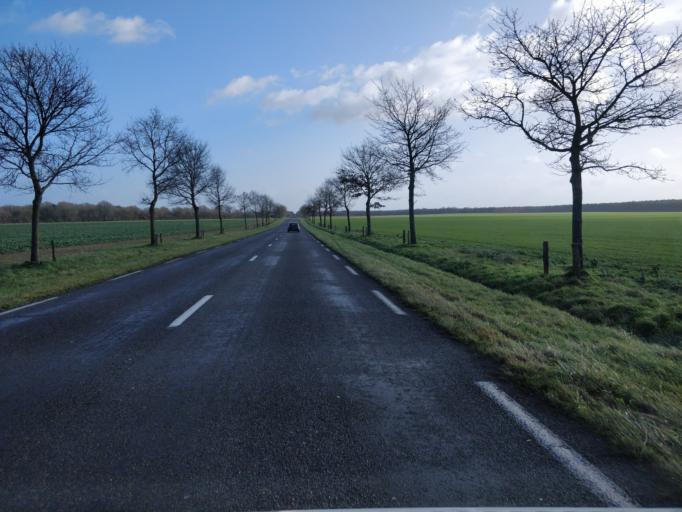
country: FR
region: Ile-de-France
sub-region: Departement de Seine-et-Marne
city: Bagneaux-sur-Loing
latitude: 48.2542
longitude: 2.7543
